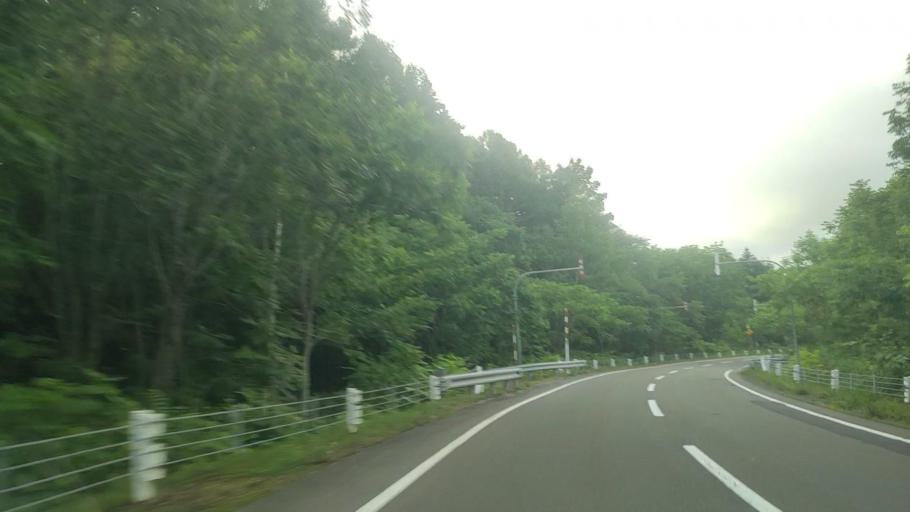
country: JP
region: Hokkaido
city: Bibai
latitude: 43.1257
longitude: 142.1017
